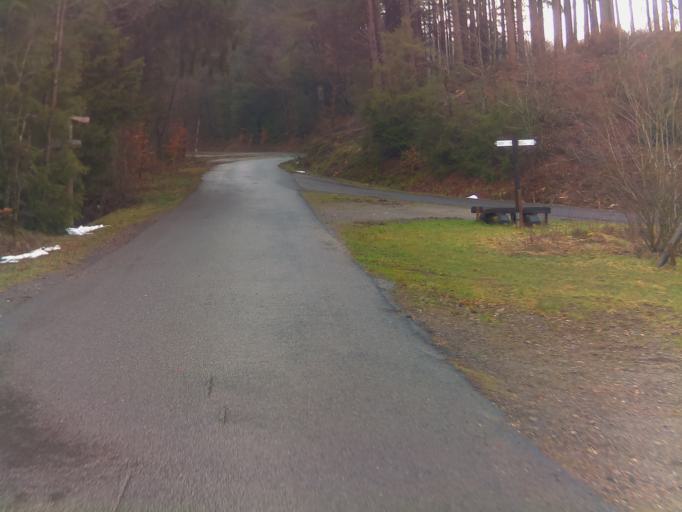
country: DE
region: Rheinland-Pfalz
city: Borfink
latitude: 49.6960
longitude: 7.0809
